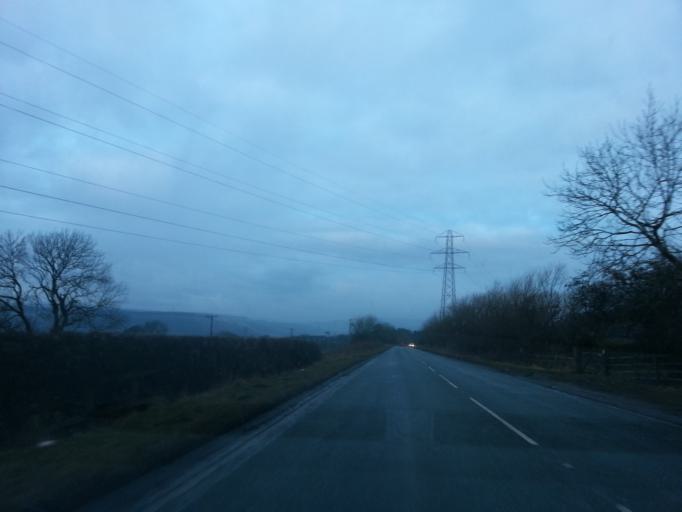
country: GB
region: England
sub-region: County Durham
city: Hamsterley
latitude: 54.7117
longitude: -1.7865
